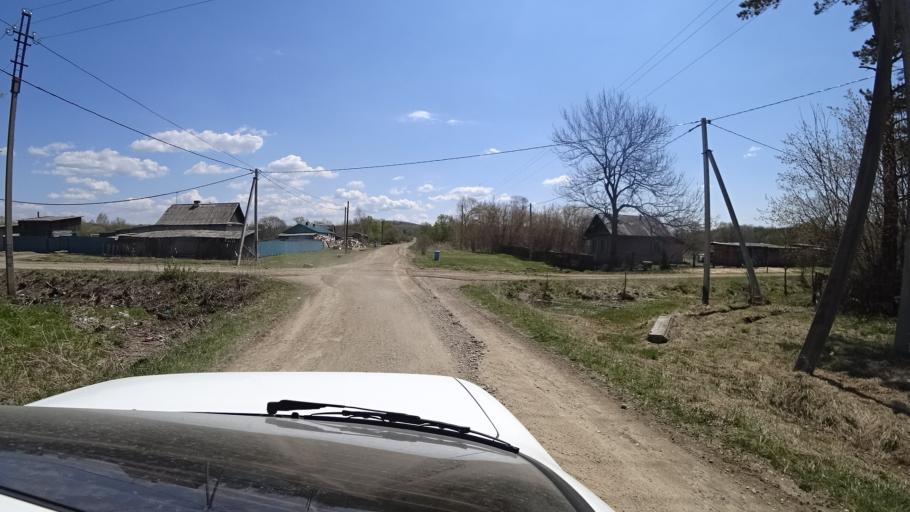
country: RU
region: Primorskiy
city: Lazo
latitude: 45.7910
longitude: 133.7649
